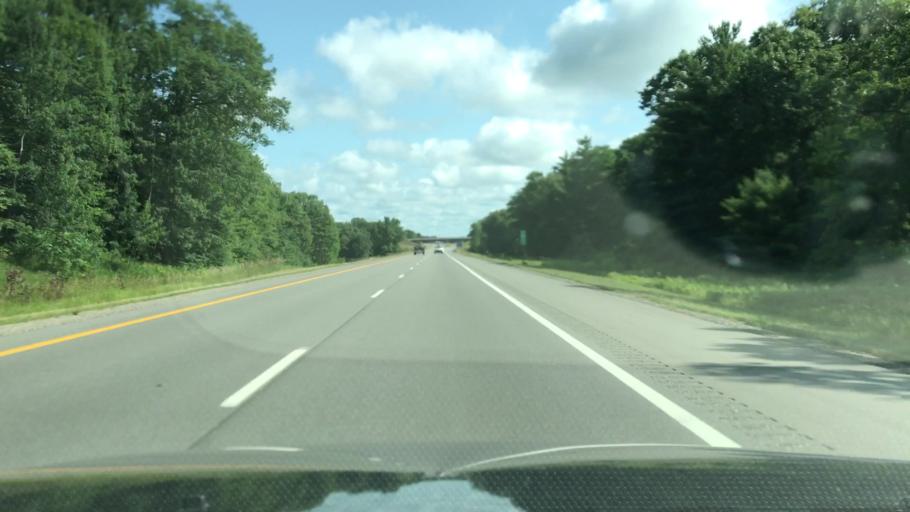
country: US
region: Michigan
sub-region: Montcalm County
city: Howard City
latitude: 43.4515
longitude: -85.4842
